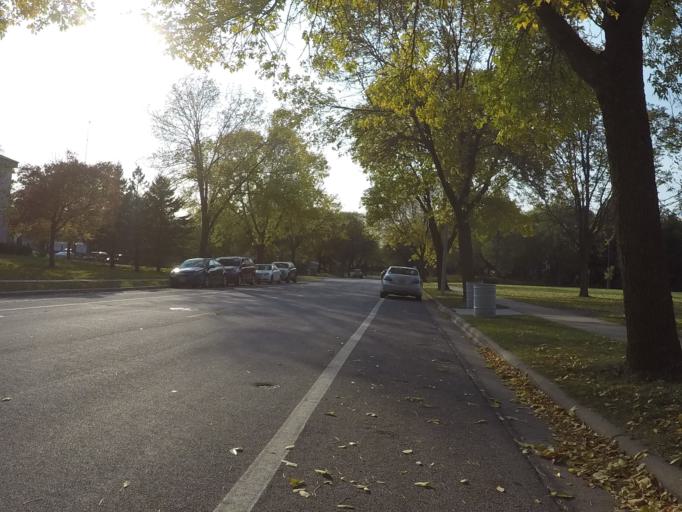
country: US
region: Wisconsin
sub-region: Dane County
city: Middleton
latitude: 43.0642
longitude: -89.5162
